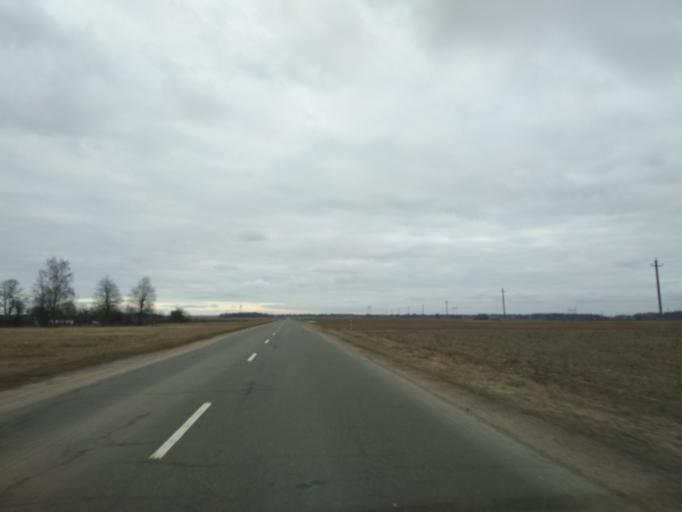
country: BY
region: Minsk
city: Mar''ina Horka
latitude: 53.5627
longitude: 28.0333
